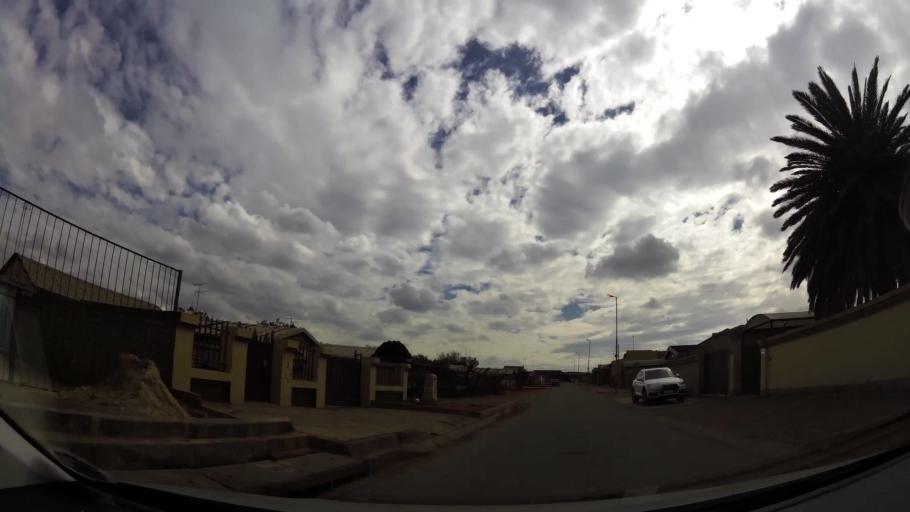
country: ZA
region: Gauteng
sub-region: City of Johannesburg Metropolitan Municipality
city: Soweto
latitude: -26.2793
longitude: 27.8486
